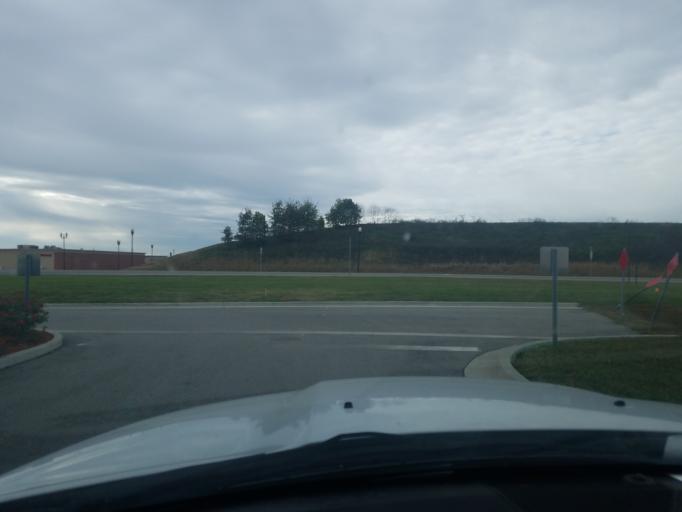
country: US
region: Indiana
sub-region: Dubois County
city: Ferdinand
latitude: 38.2106
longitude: -86.8646
